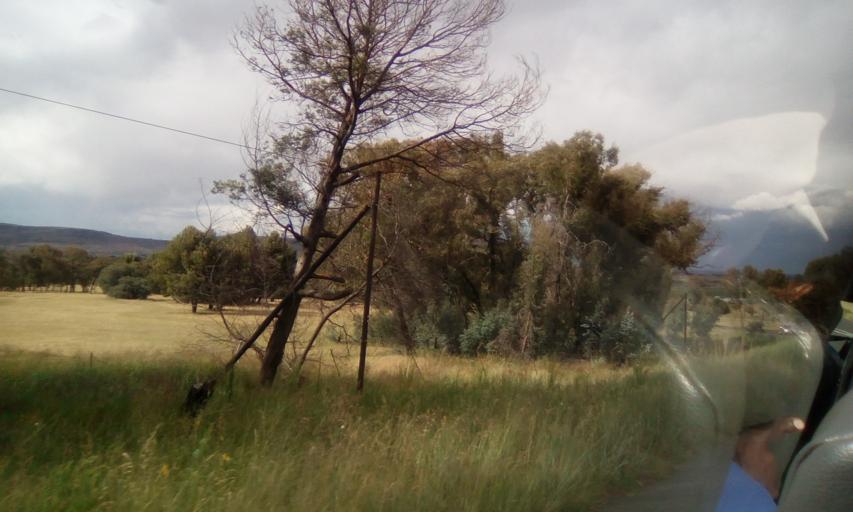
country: ZA
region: Orange Free State
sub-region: Thabo Mofutsanyana District Municipality
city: Ladybrand
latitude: -29.2117
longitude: 27.4654
